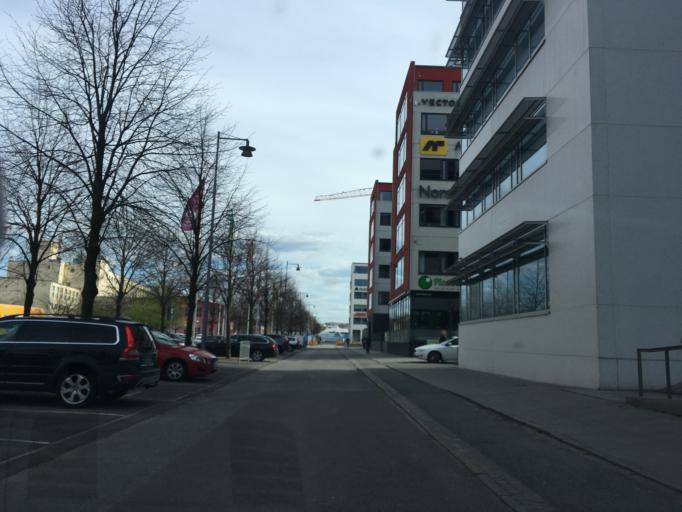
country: SE
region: Vaestra Goetaland
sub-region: Goteborg
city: Goeteborg
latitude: 57.7080
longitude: 11.9434
